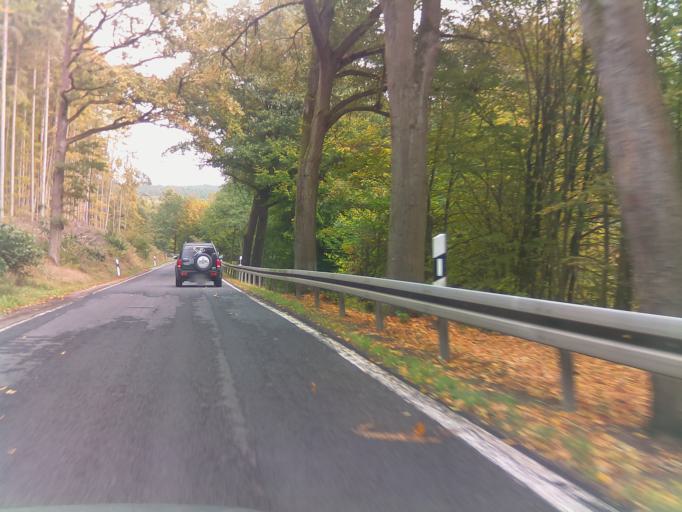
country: DE
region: Thuringia
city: Unterkatz
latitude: 50.6269
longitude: 10.2713
